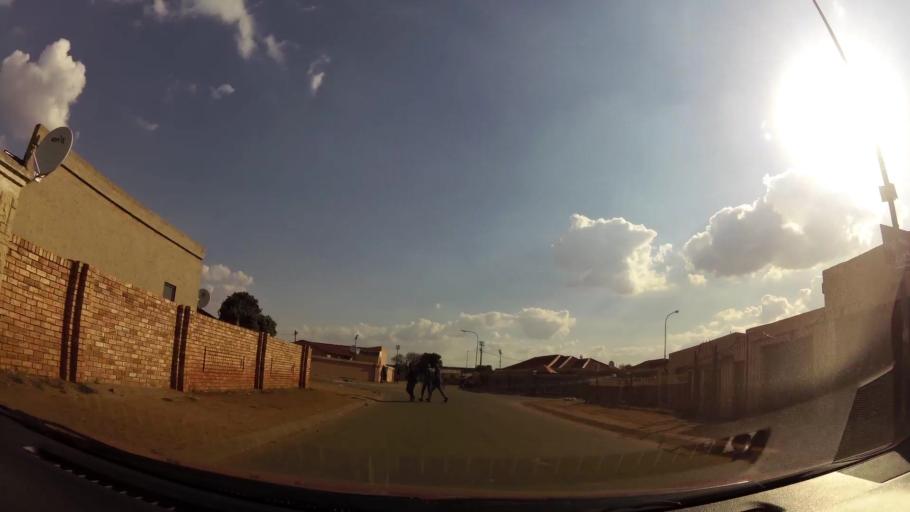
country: ZA
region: Gauteng
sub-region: City of Johannesburg Metropolitan Municipality
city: Soweto
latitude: -26.2257
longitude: 27.8701
